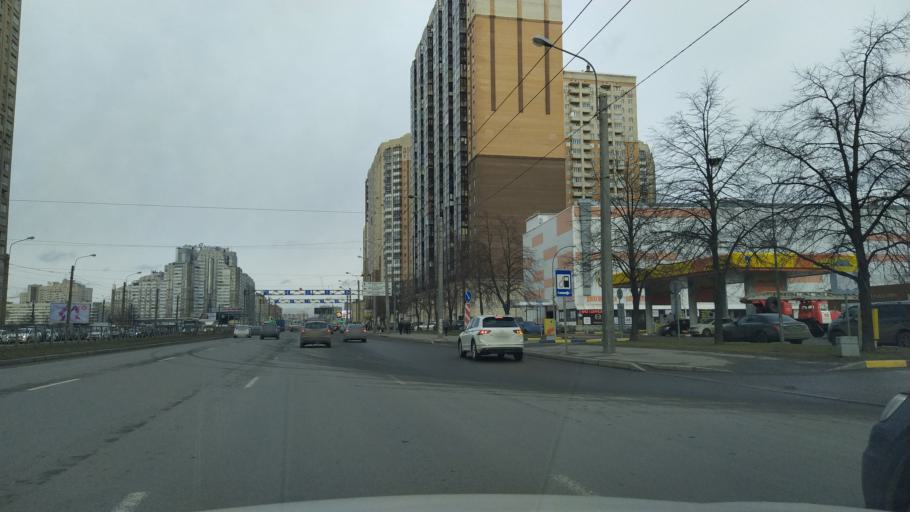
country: RU
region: Leningrad
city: Chernaya Rechka
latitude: 59.9985
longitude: 30.2997
